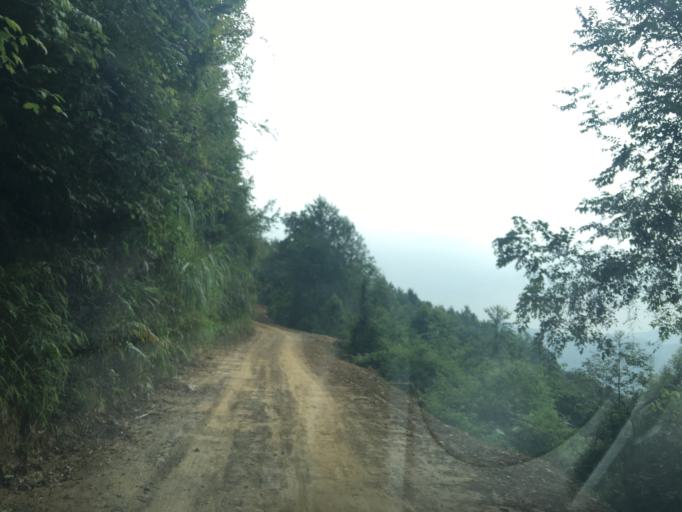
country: CN
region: Guangxi Zhuangzu Zizhiqu
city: Xinzhou
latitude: 25.1617
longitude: 105.6867
